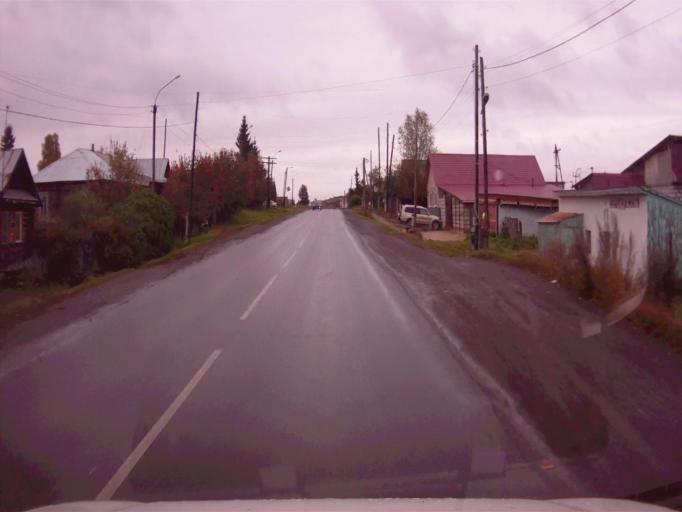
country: RU
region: Chelyabinsk
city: Verkhniy Ufaley
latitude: 56.0545
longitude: 60.2044
